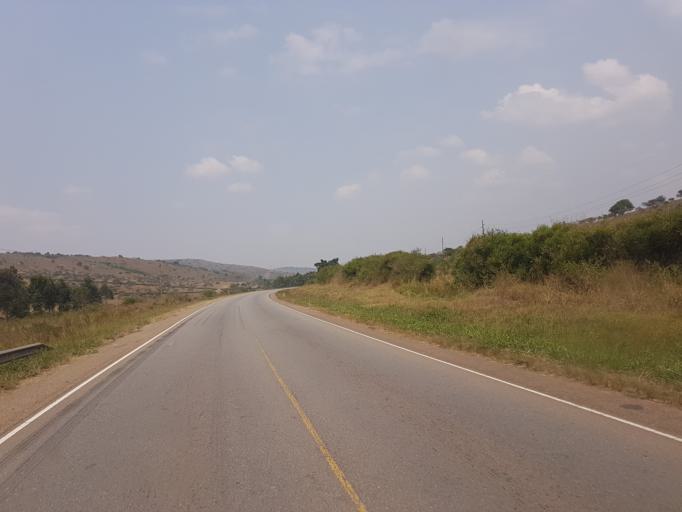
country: UG
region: Western Region
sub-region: Mbarara District
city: Mbarara
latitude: -0.4862
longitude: 30.8710
